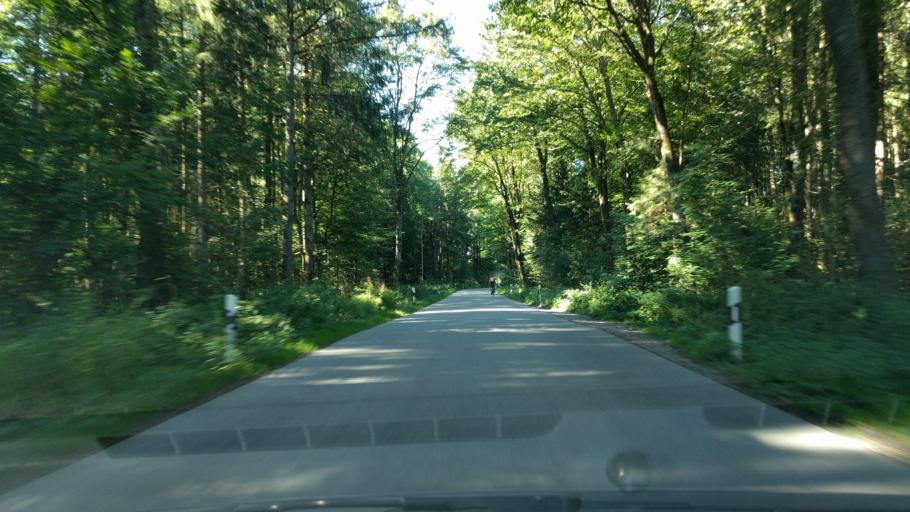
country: DE
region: Bavaria
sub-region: Upper Bavaria
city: Grunwald
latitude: 48.0353
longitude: 11.5505
